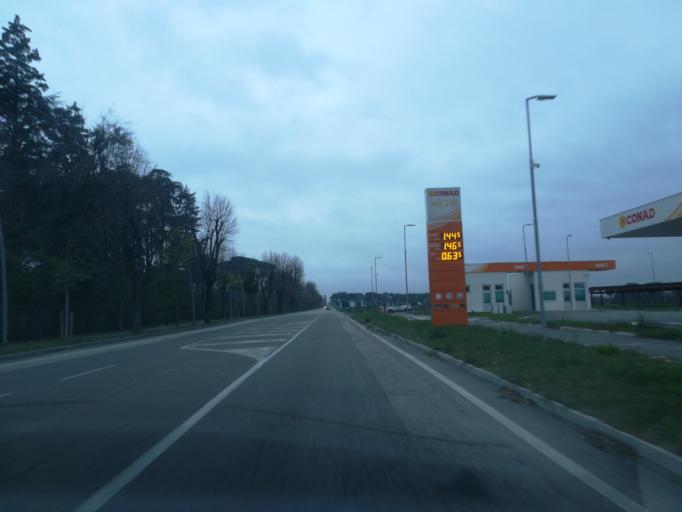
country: IT
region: Emilia-Romagna
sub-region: Provincia di Bologna
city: Imola
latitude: 44.3667
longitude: 11.6804
